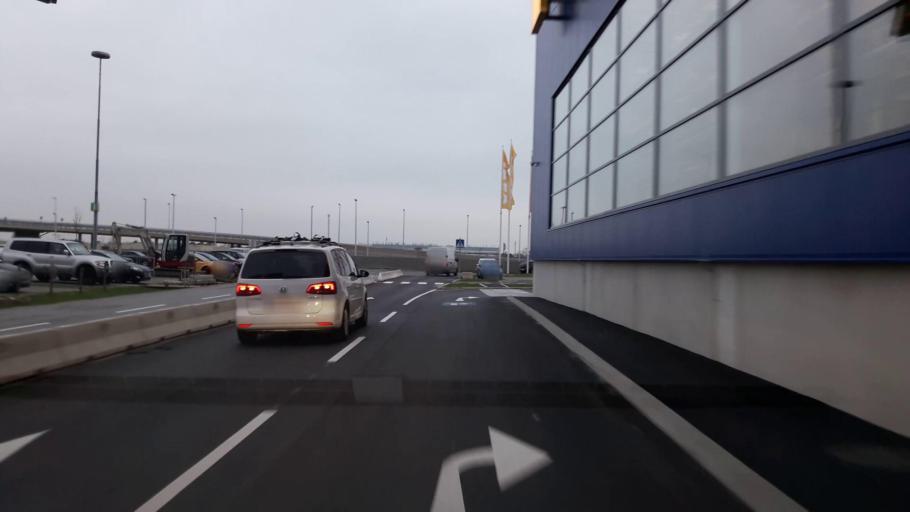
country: AT
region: Lower Austria
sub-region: Politischer Bezirk Wien-Umgebung
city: Gerasdorf bei Wien
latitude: 48.2553
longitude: 16.4723
